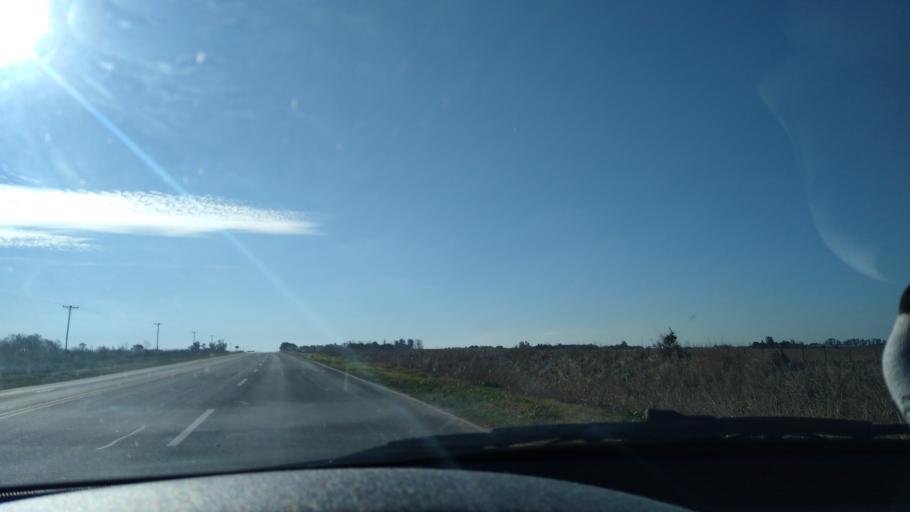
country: AR
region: Entre Rios
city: Aranguren
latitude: -32.4011
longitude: -60.3260
